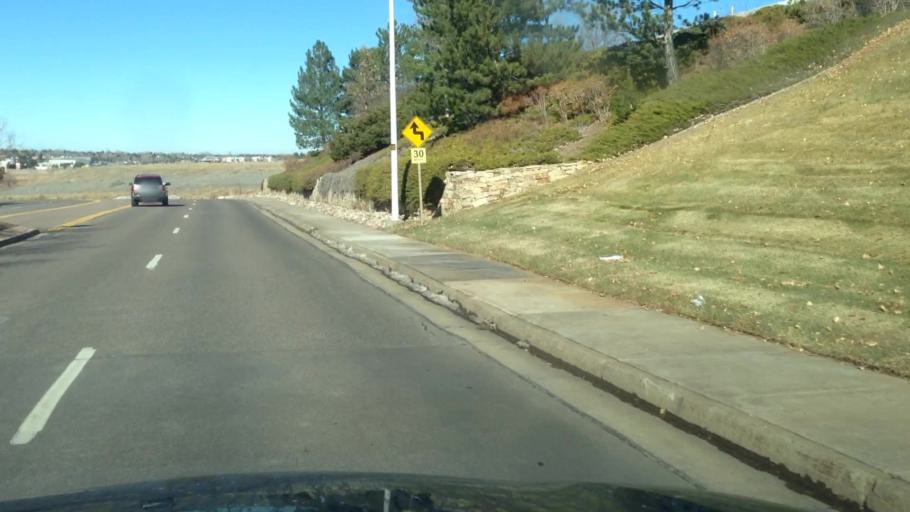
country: US
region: Colorado
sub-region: Arapahoe County
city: Centennial
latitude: 39.5809
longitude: -104.8567
